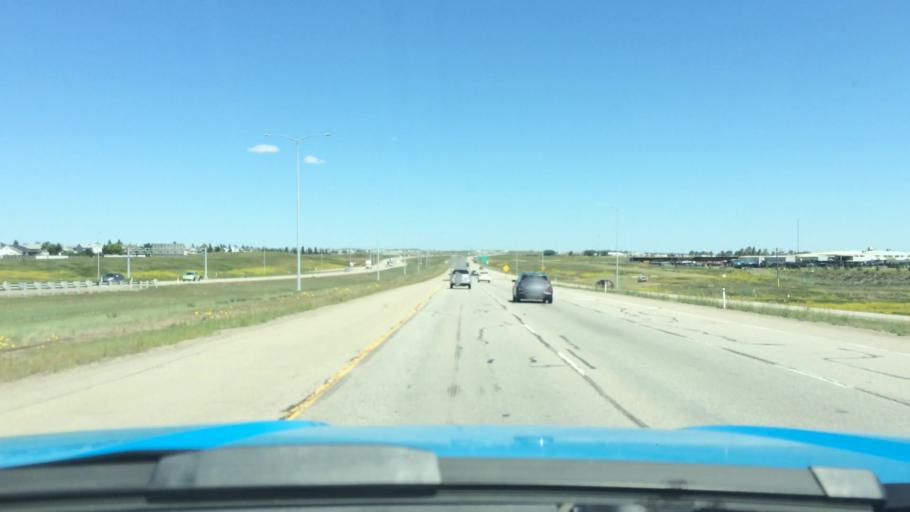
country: CA
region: Alberta
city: Chestermere
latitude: 51.0691
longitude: -113.9202
